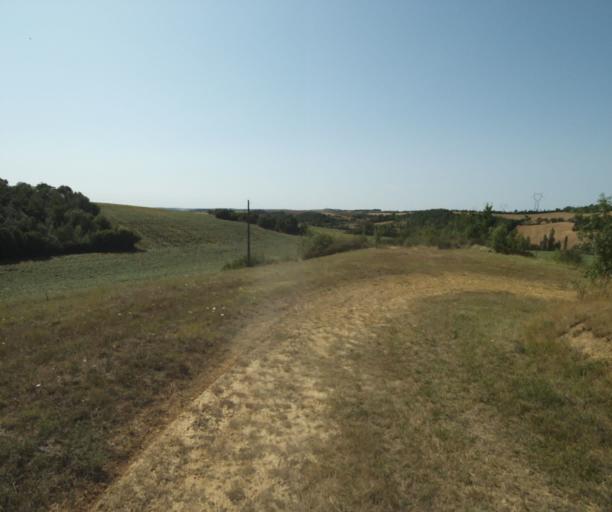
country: FR
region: Midi-Pyrenees
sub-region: Departement de la Haute-Garonne
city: Saint-Felix-Lauragais
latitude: 43.4448
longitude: 1.8403
